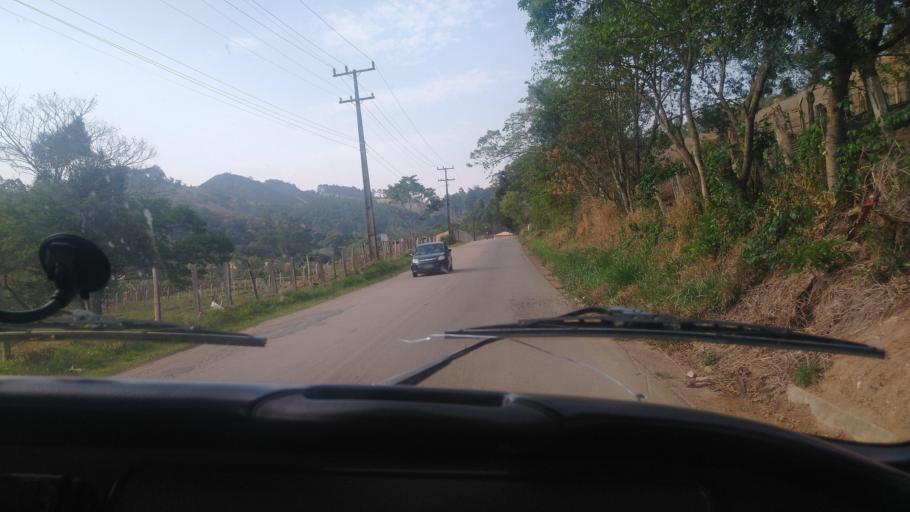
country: BR
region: Minas Gerais
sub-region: Extrema
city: Extrema
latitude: -22.7801
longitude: -46.4414
